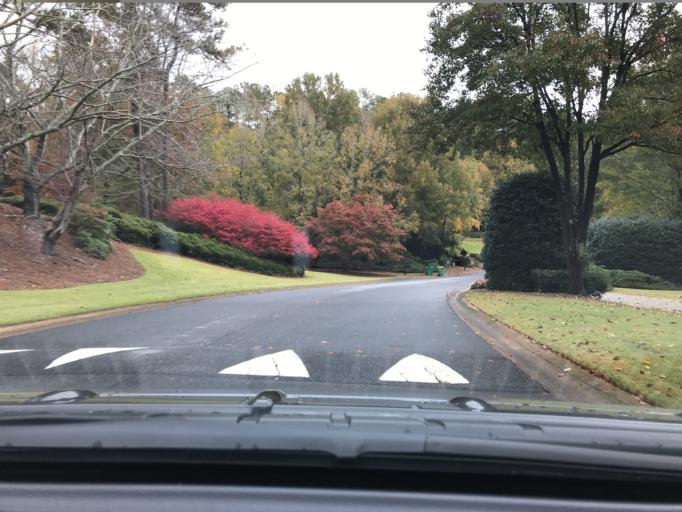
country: US
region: Georgia
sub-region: Fulton County
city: Johns Creek
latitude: 34.0054
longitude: -84.2418
